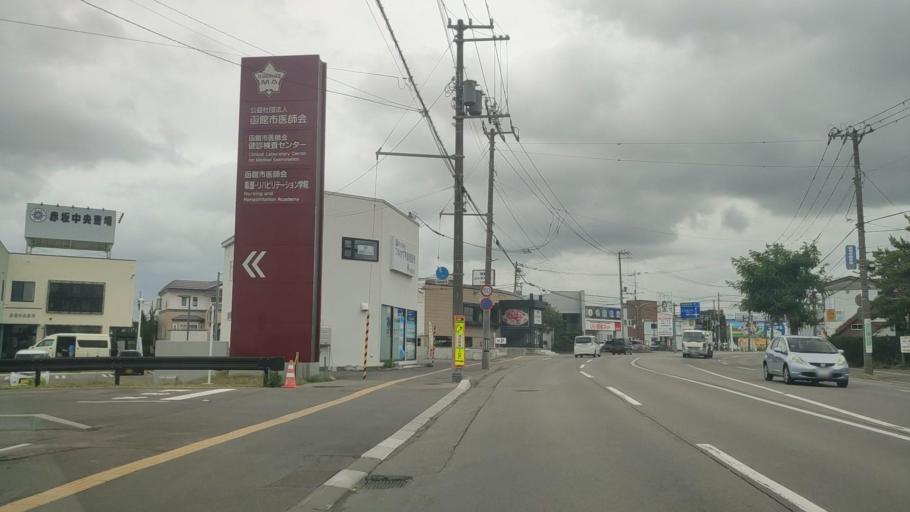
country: JP
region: Hokkaido
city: Hakodate
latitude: 41.7988
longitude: 140.7504
